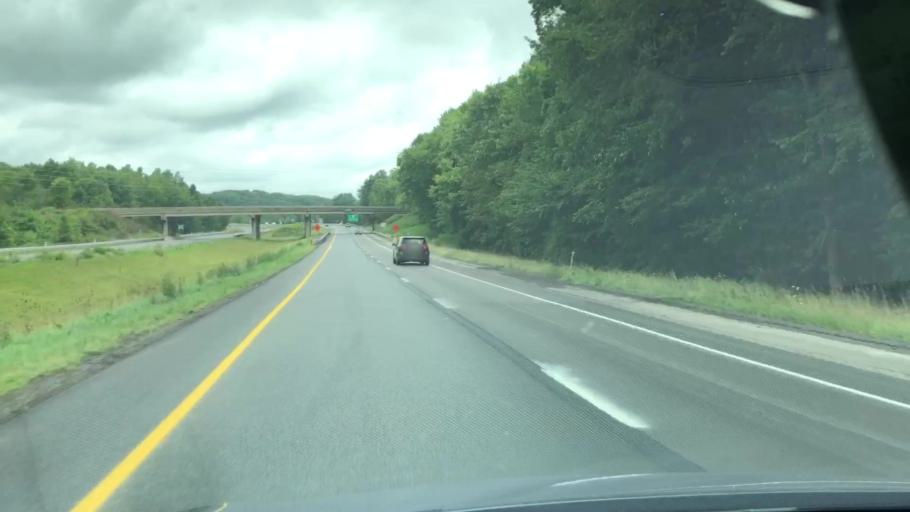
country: US
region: Pennsylvania
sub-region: Butler County
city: Prospect
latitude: 40.9556
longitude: -80.1395
